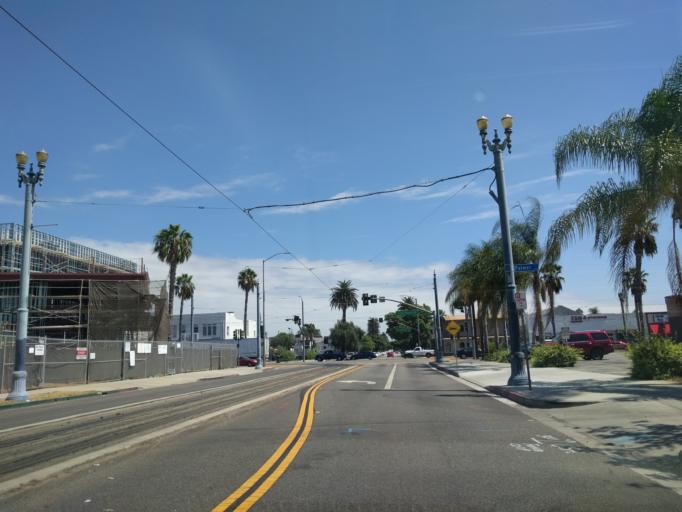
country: US
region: California
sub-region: Los Angeles County
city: Long Beach
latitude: 33.7765
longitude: -118.1902
